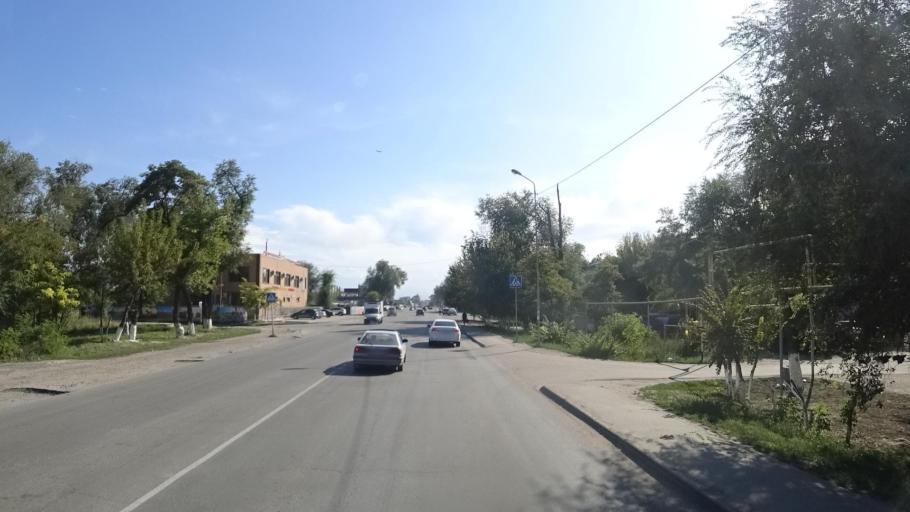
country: KZ
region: Almaty Oblysy
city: Energeticheskiy
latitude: 43.4242
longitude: 77.0242
